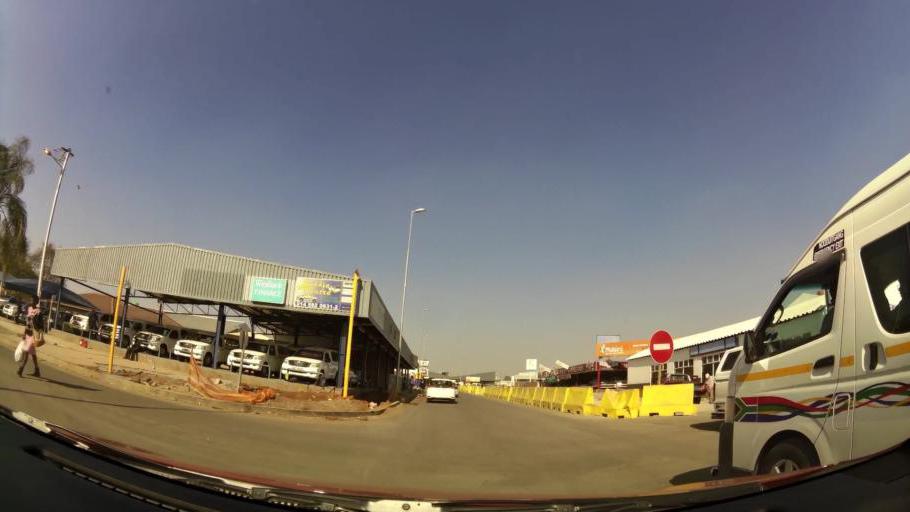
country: ZA
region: North-West
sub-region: Bojanala Platinum District Municipality
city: Rustenburg
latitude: -25.6639
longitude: 27.2413
